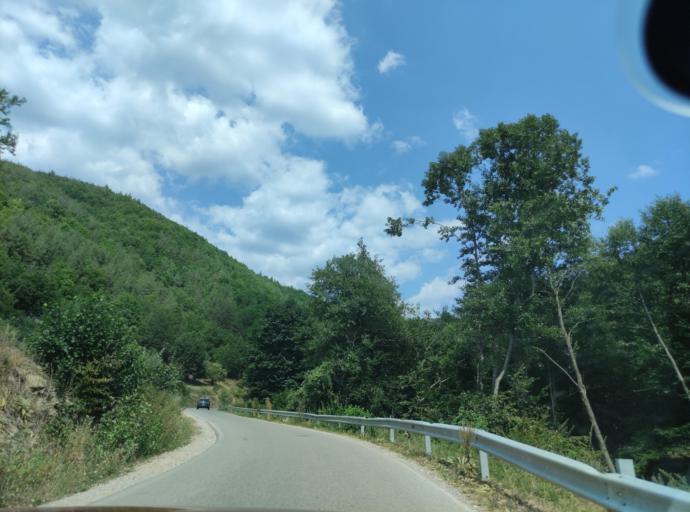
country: BG
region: Blagoevgrad
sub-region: Obshtina Belitsa
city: Belitsa
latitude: 42.0027
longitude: 23.5512
